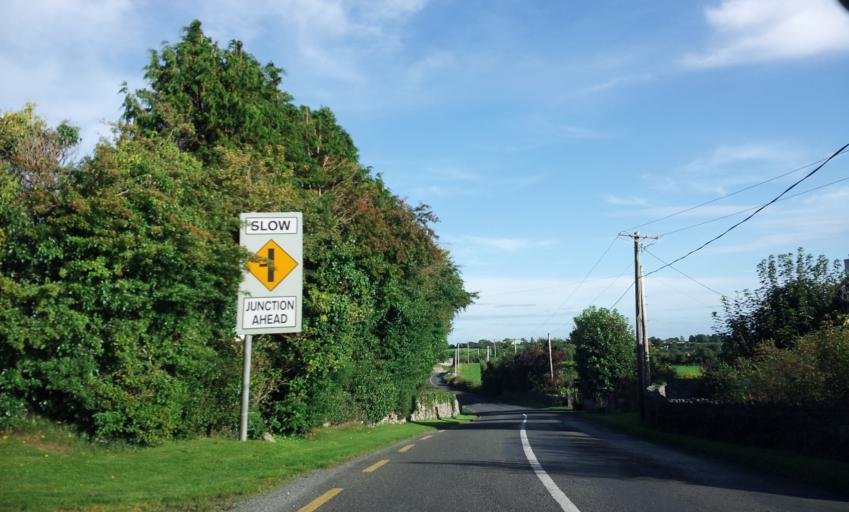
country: IE
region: Munster
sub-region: An Clar
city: Ennis
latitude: 52.9718
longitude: -9.0884
